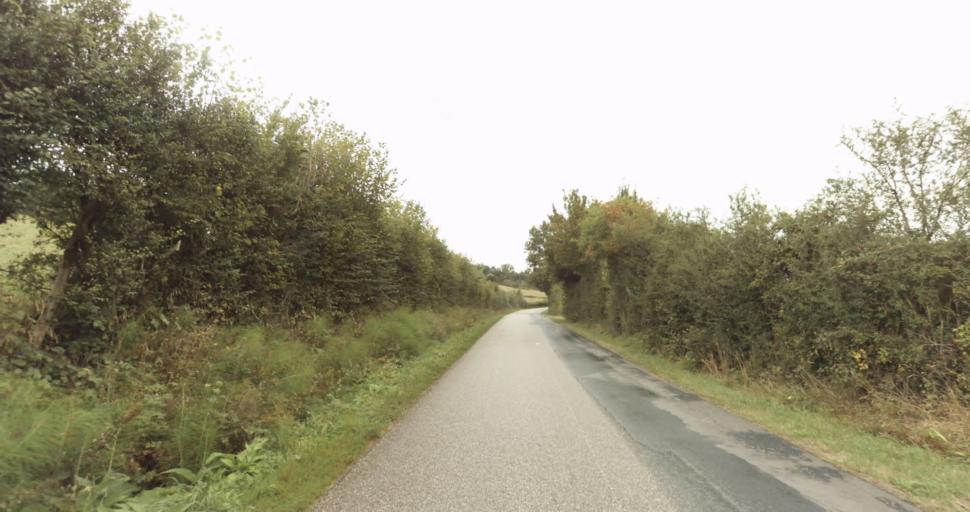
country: FR
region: Lower Normandy
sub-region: Departement de l'Orne
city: Vimoutiers
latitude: 48.8727
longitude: 0.2222
